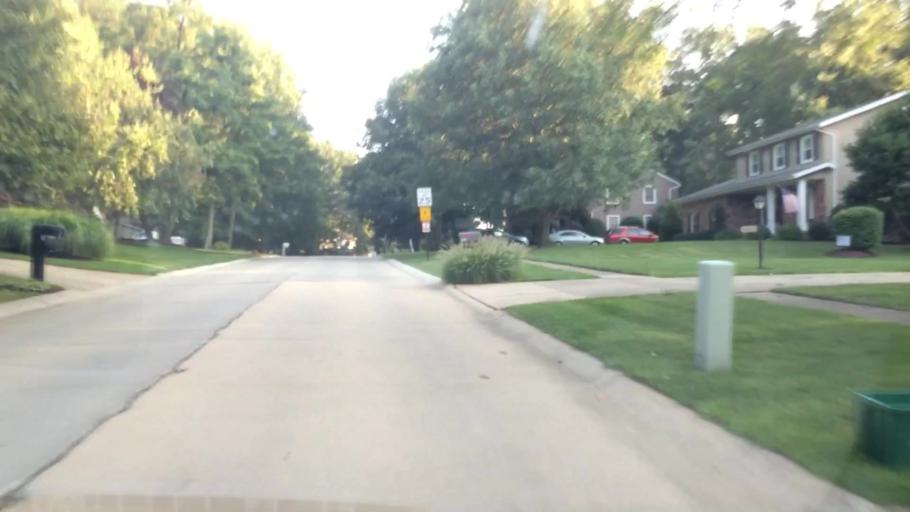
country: US
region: Ohio
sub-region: Summit County
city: Silver Lake
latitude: 41.1828
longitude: -81.4569
